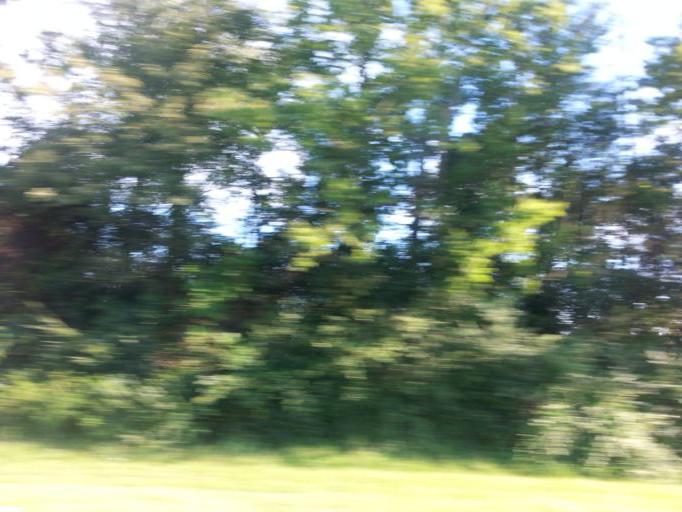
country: US
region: Alabama
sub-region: Lauderdale County
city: Killen
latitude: 34.8606
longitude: -87.4678
